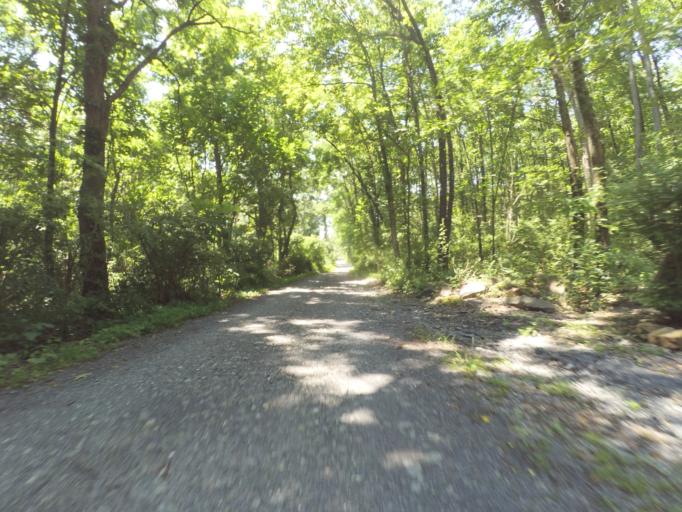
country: US
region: Pennsylvania
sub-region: Centre County
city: Pleasant Gap
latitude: 40.8249
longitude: -77.7384
